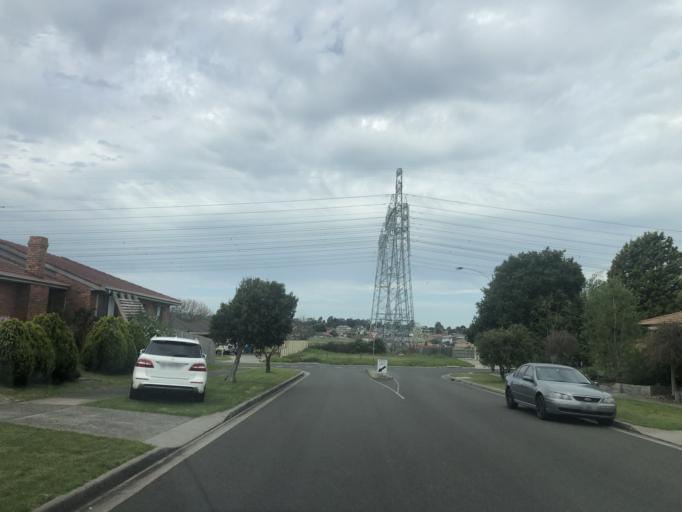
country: AU
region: Victoria
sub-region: Casey
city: Hallam
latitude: -38.0064
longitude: 145.2826
